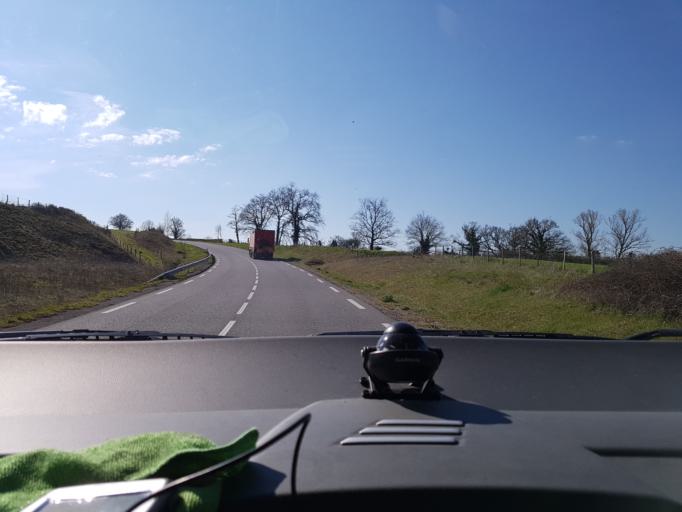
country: FR
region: Midi-Pyrenees
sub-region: Departement de l'Aveyron
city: Moyrazes
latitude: 44.3753
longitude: 2.4592
